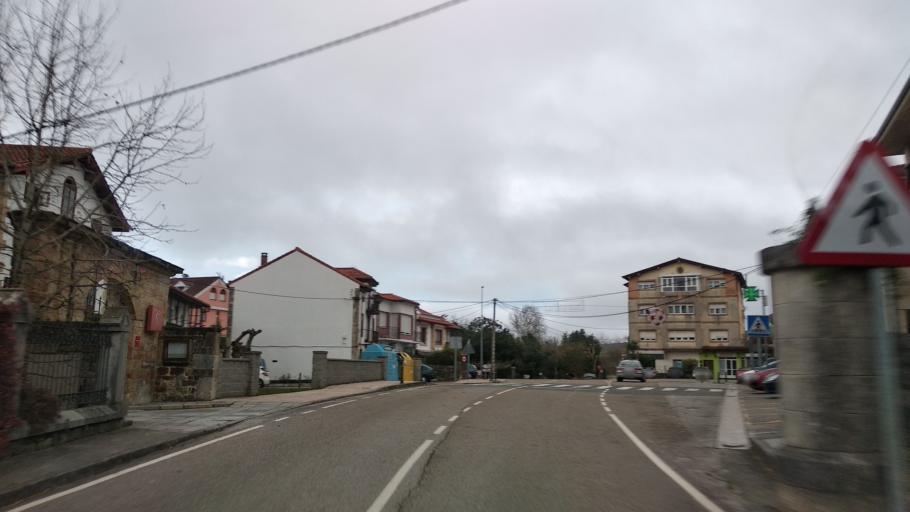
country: ES
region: Cantabria
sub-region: Provincia de Cantabria
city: Entrambasaguas
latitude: 43.4123
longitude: -3.6989
